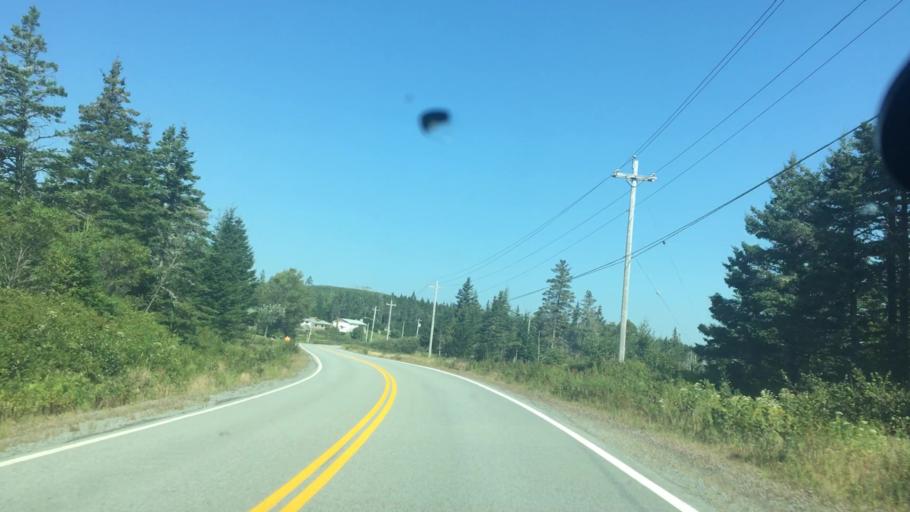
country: CA
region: Nova Scotia
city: New Glasgow
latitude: 44.9251
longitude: -62.2981
